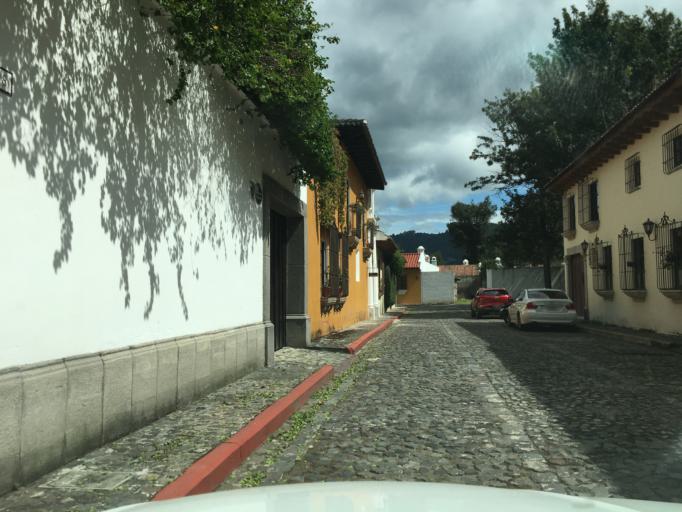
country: GT
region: Sacatepequez
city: Antigua Guatemala
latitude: 14.5487
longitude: -90.7380
